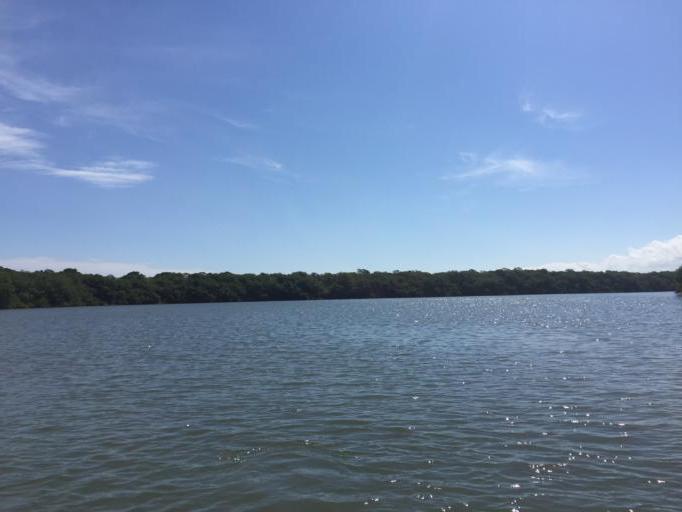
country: MX
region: Veracruz
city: Tecolutla
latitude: 20.4656
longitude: -97.0000
